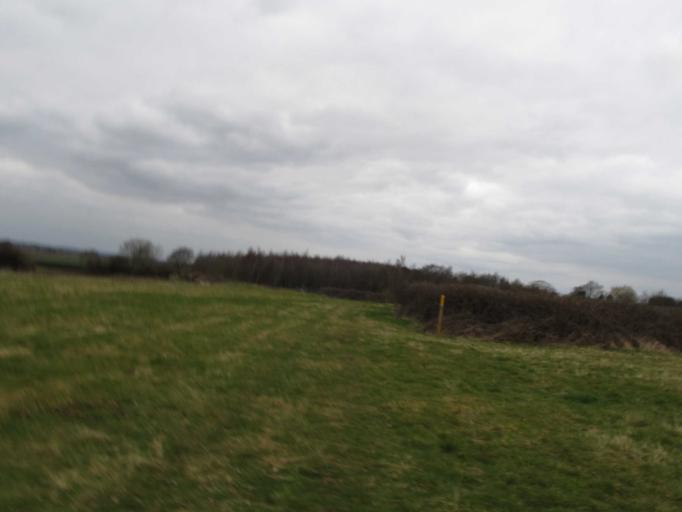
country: GB
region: England
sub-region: Nottinghamshire
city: Retford
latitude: 53.3833
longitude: -0.9086
